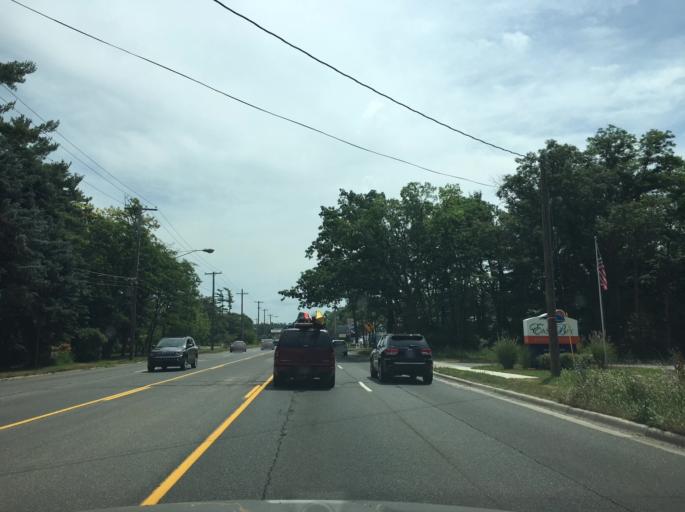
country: US
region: Michigan
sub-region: Grand Traverse County
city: Traverse City
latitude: 44.7507
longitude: -85.5630
